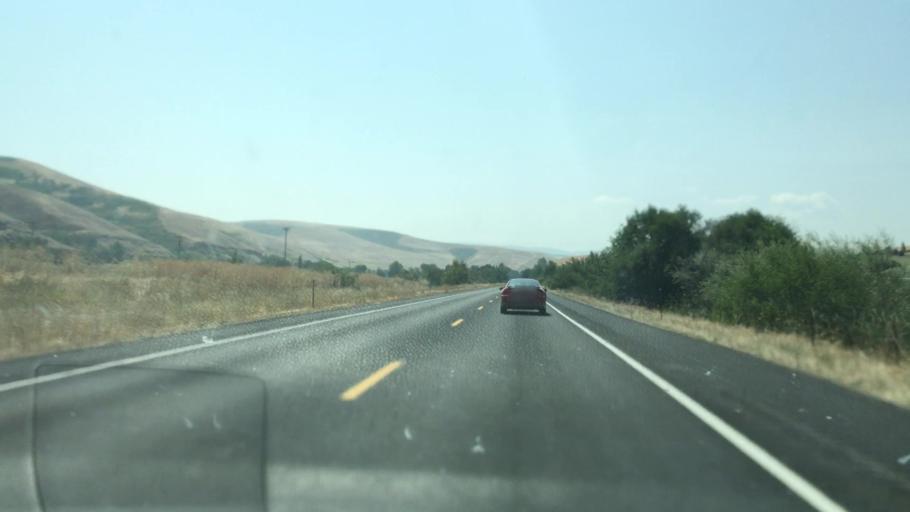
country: US
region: Idaho
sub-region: Nez Perce County
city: Lapwai
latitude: 46.4355
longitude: -116.8087
